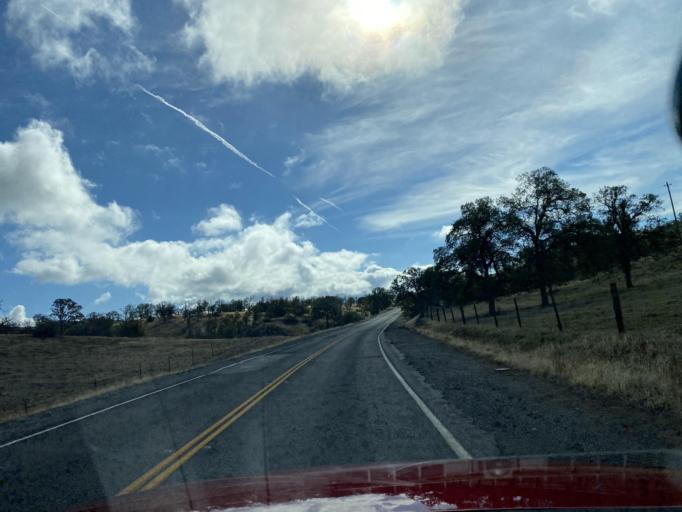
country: US
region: California
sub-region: Glenn County
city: Willows
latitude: 39.4831
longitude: -122.5161
